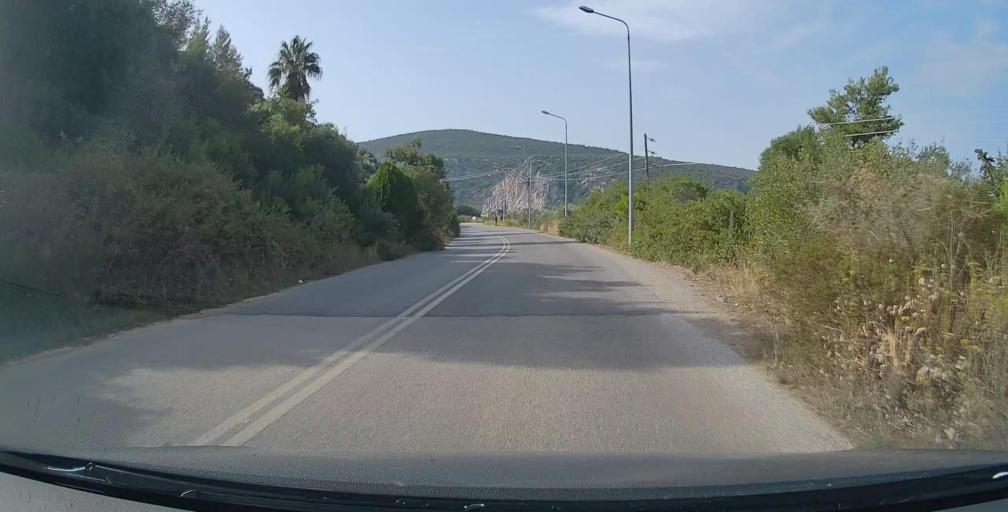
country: GR
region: Central Macedonia
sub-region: Nomos Chalkidikis
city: Sykia
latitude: 39.9656
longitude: 23.9267
